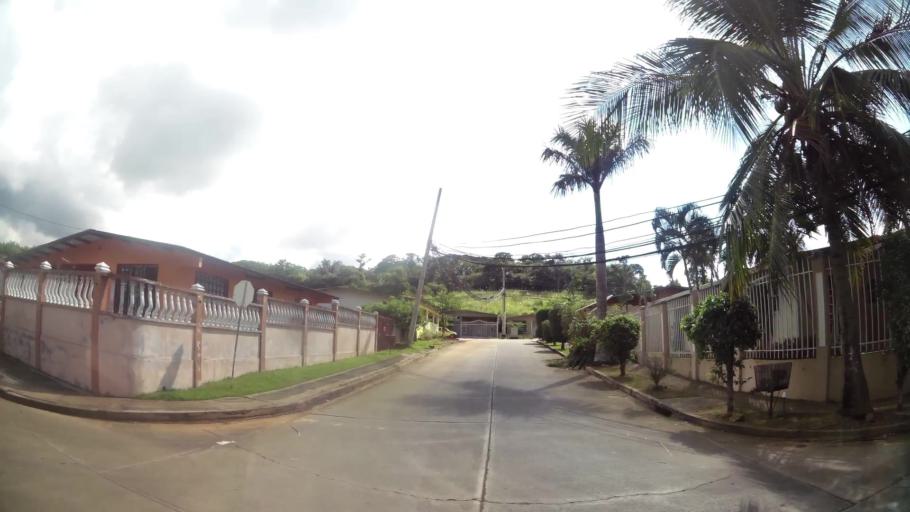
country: PA
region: Panama
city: Nuevo Arraijan
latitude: 8.9137
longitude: -79.7406
